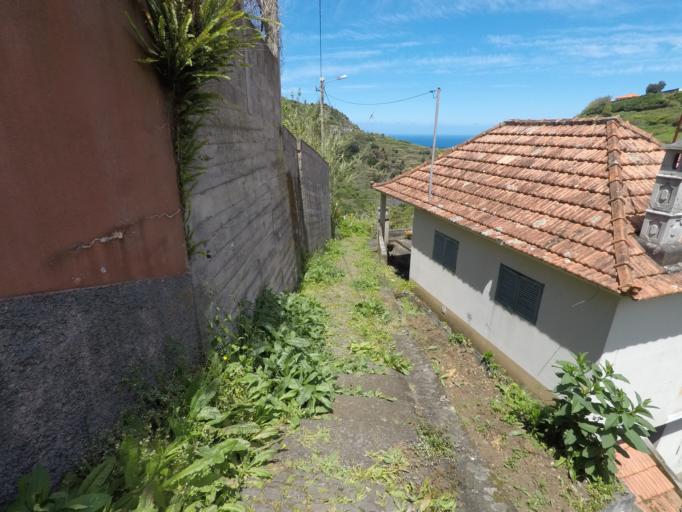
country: PT
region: Madeira
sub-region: Sao Vicente
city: Sao Vicente
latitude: 32.8206
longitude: -16.9740
